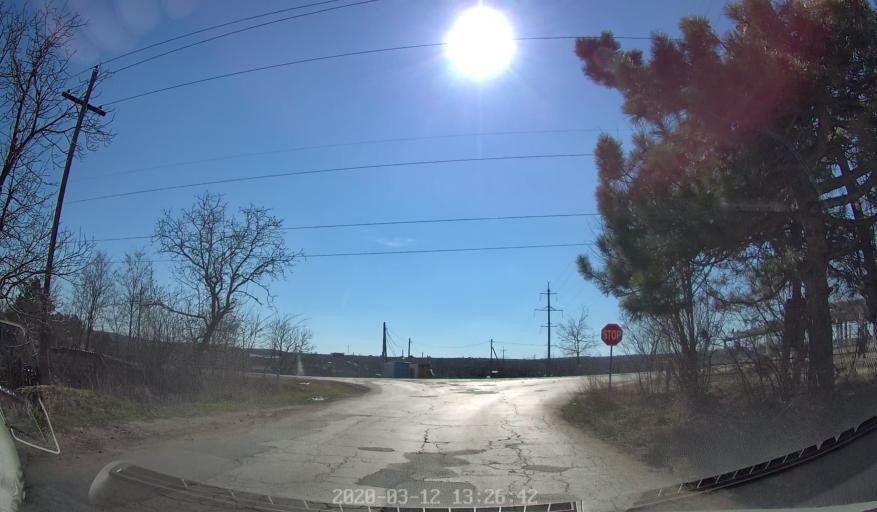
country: MD
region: Laloveni
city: Ialoveni
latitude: 46.9323
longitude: 28.8137
